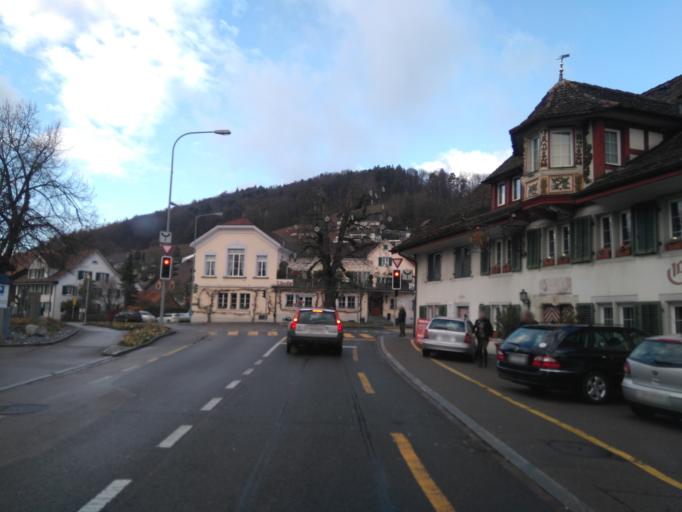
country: CH
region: Zurich
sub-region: Bezirk Dietikon
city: Weiningen
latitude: 47.4194
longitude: 8.4349
